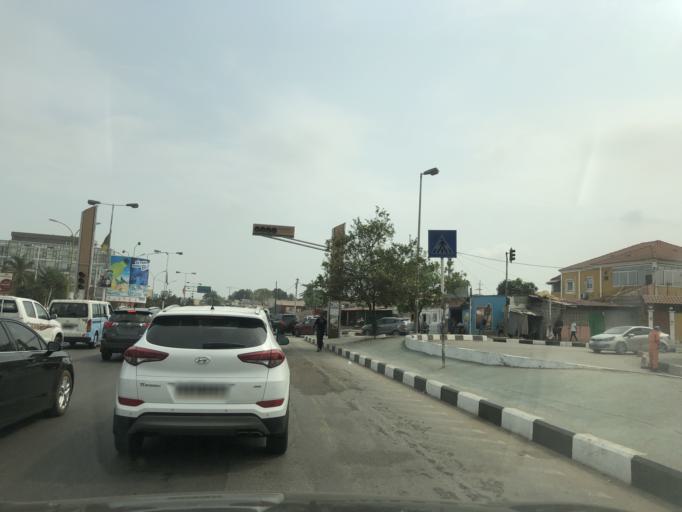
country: AO
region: Luanda
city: Luanda
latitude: -8.8473
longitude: 13.2119
